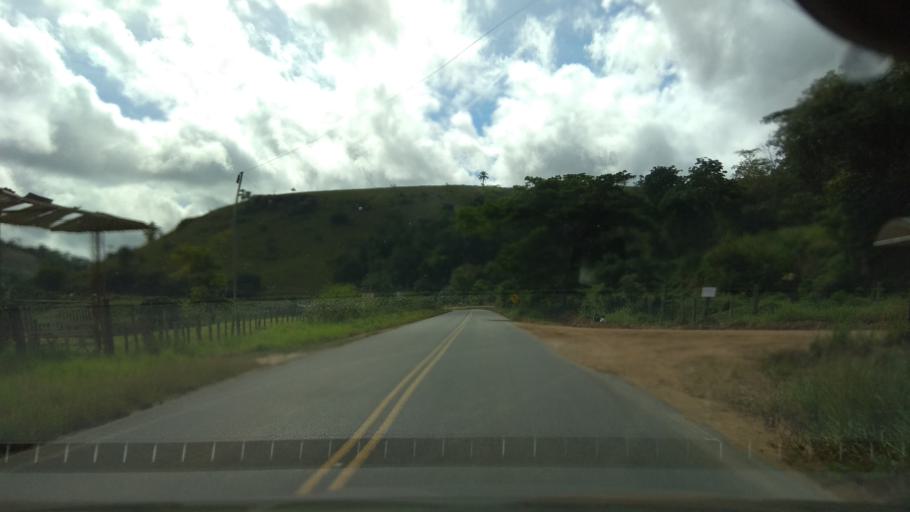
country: BR
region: Bahia
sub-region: Mutuipe
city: Mutuipe
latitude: -13.1908
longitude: -39.4430
